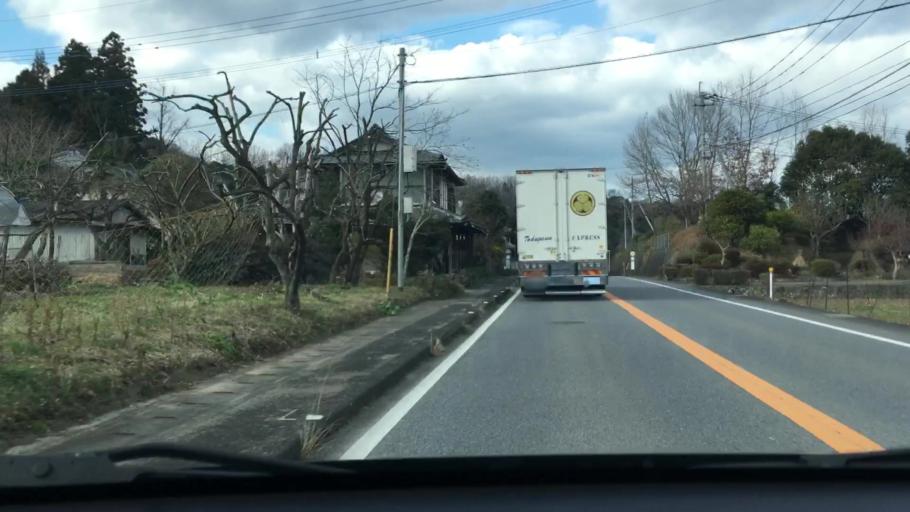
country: JP
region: Oita
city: Usuki
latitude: 33.0202
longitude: 131.6980
